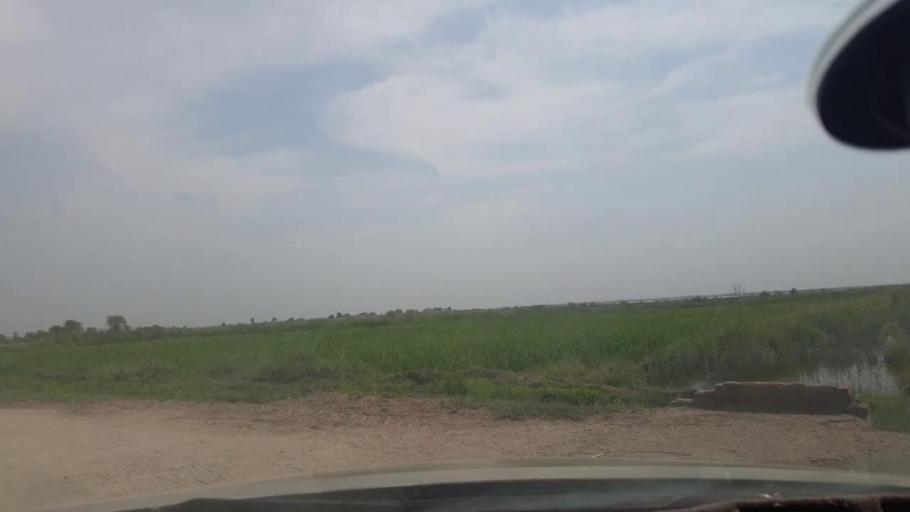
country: PK
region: Sindh
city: Jacobabad
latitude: 28.3112
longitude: 68.4829
